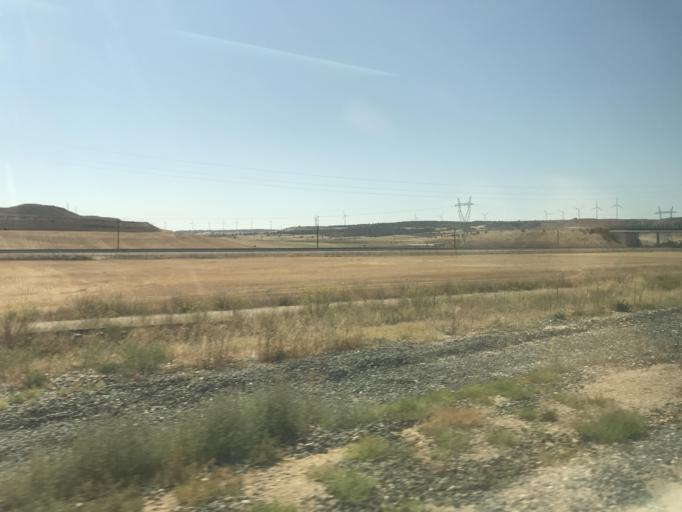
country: ES
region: Castille and Leon
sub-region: Provincia de Palencia
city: Torquemada
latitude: 42.0169
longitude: -4.2972
